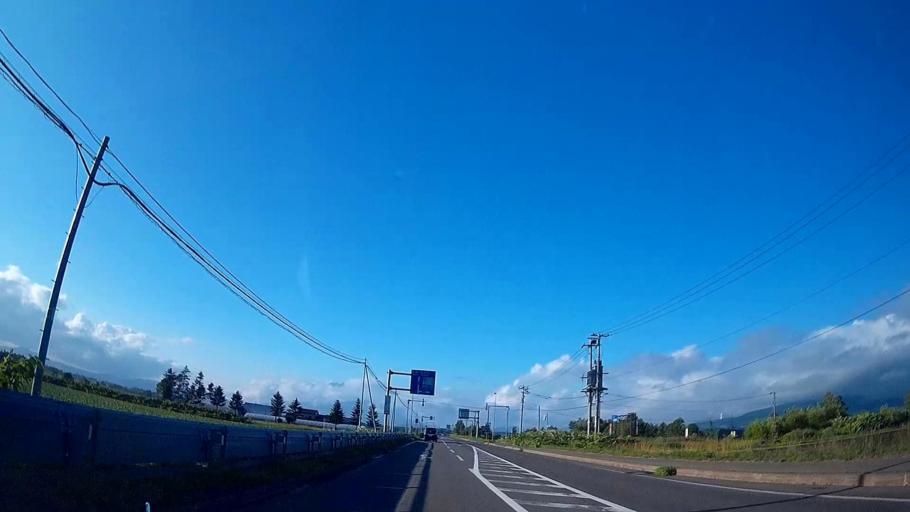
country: JP
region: Hokkaido
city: Date
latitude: 42.6420
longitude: 140.8033
